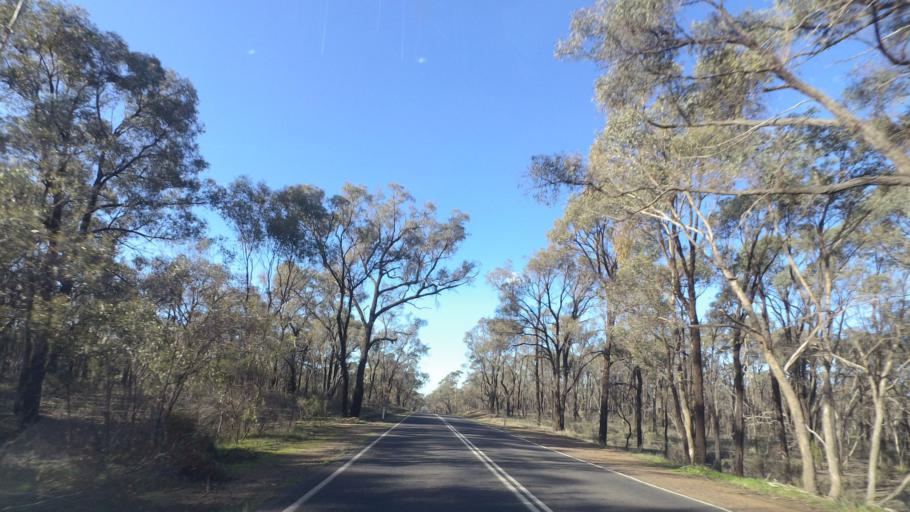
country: AU
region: Victoria
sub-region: Greater Bendigo
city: Epsom
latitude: -36.6649
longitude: 144.4421
